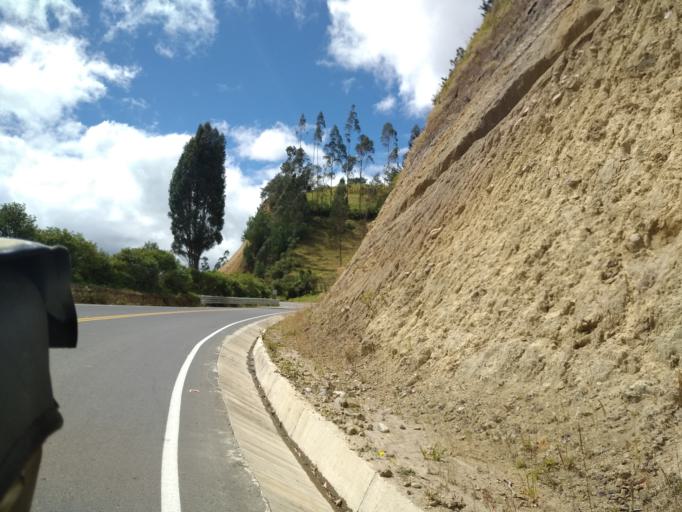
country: EC
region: Cotopaxi
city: Saquisili
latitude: -0.7295
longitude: -78.8998
